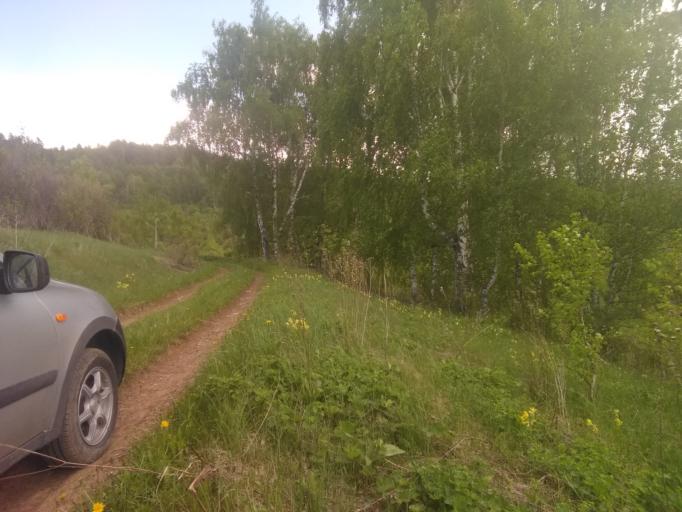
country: RU
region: Chelyabinsk
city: Sim
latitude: 55.0017
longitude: 57.7221
